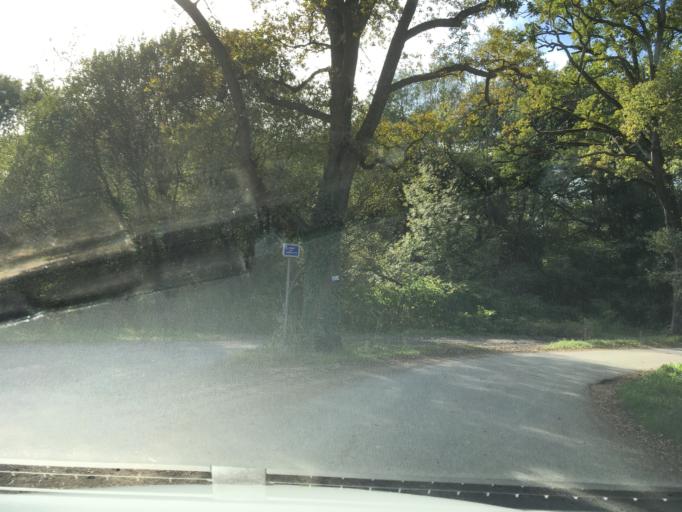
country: FR
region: Aquitaine
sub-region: Departement des Pyrenees-Atlantiques
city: Montardon
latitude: 43.3398
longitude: -0.3698
